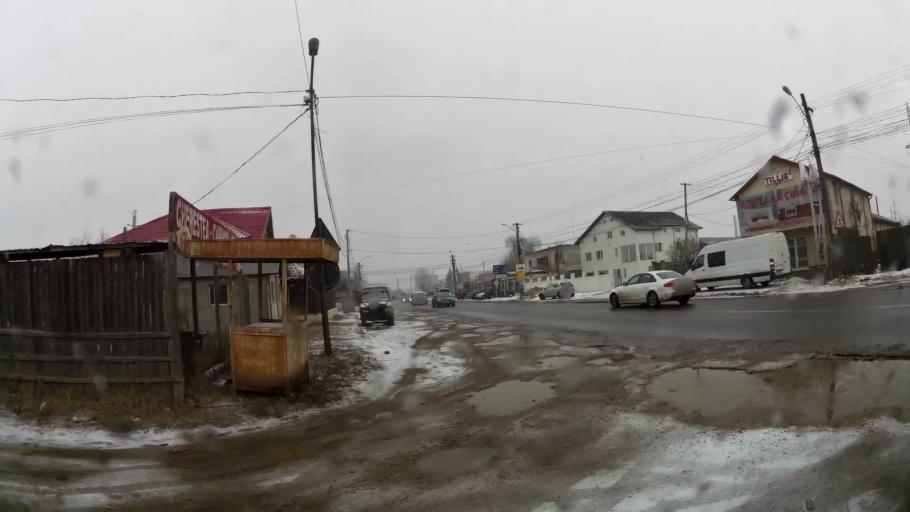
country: RO
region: Dambovita
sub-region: Municipiul Targoviste
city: Targoviste
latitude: 44.9284
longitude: 25.4306
